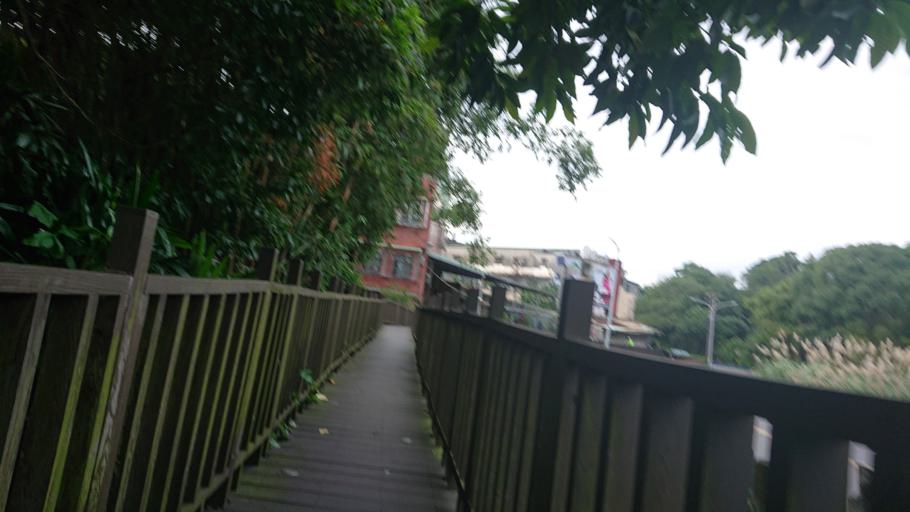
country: TW
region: Taipei
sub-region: Taipei
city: Banqiao
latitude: 24.9626
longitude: 121.4426
